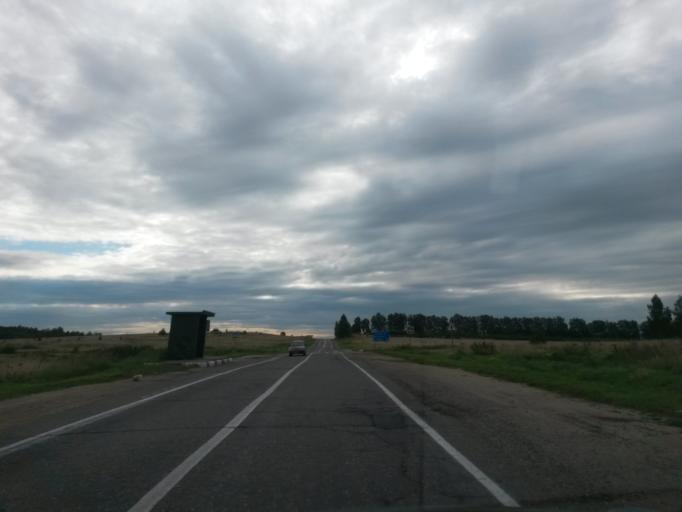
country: RU
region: Jaroslavl
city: Gavrilov-Yam
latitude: 57.3601
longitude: 39.7681
